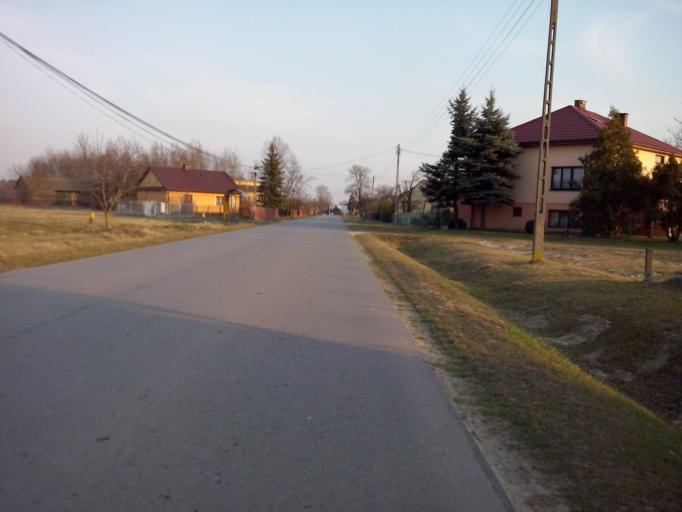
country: PL
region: Subcarpathian Voivodeship
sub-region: Powiat nizanski
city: Krzeszow
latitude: 50.3982
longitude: 22.3557
